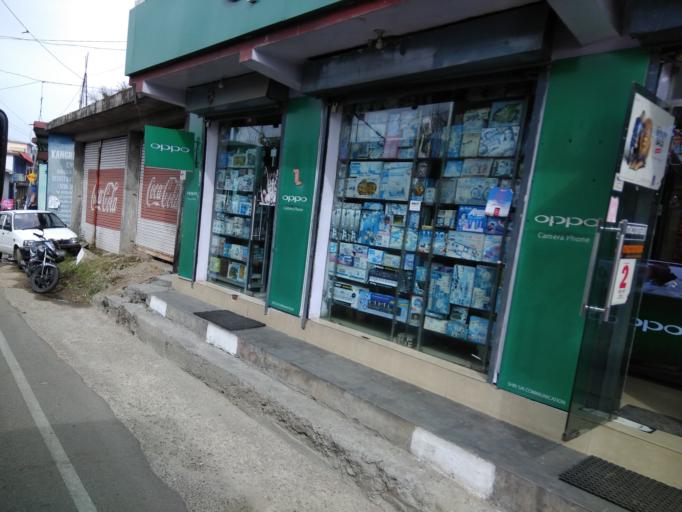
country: IN
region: Himachal Pradesh
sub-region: Kangra
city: Dharmsala
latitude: 32.1970
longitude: 76.3416
